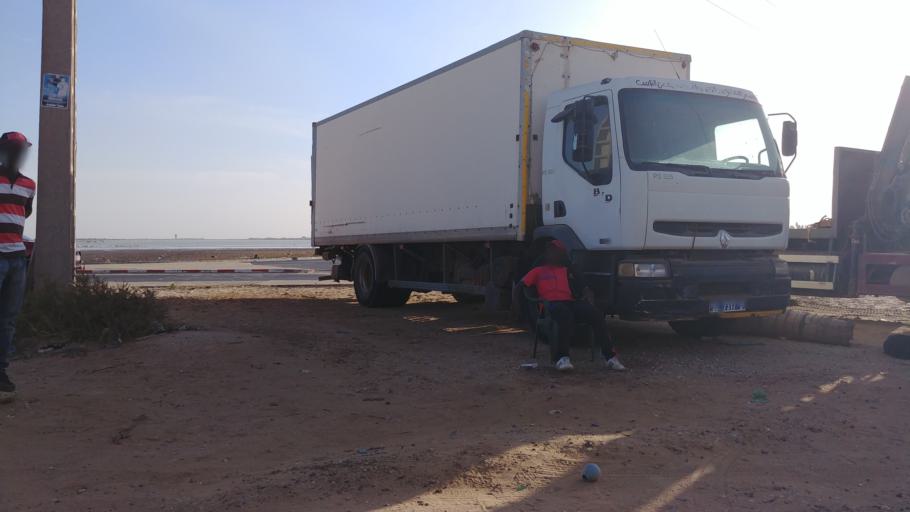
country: SN
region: Saint-Louis
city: Saint-Louis
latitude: 16.0267
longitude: -16.4784
